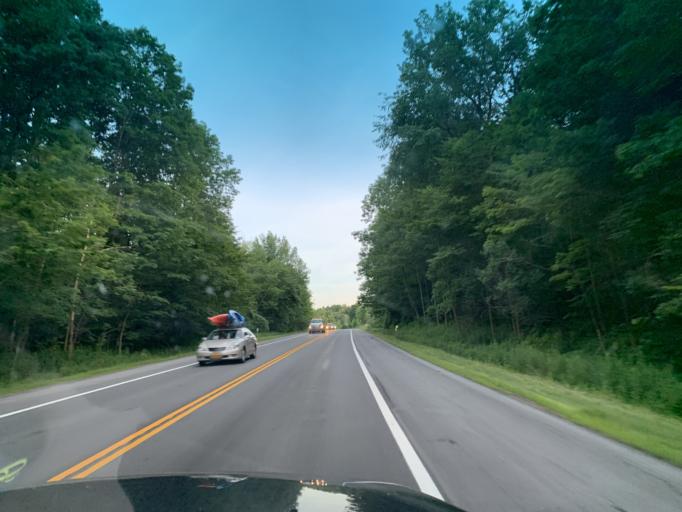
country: US
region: New York
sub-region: Oneida County
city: Chadwicks
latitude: 42.9718
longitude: -75.2522
